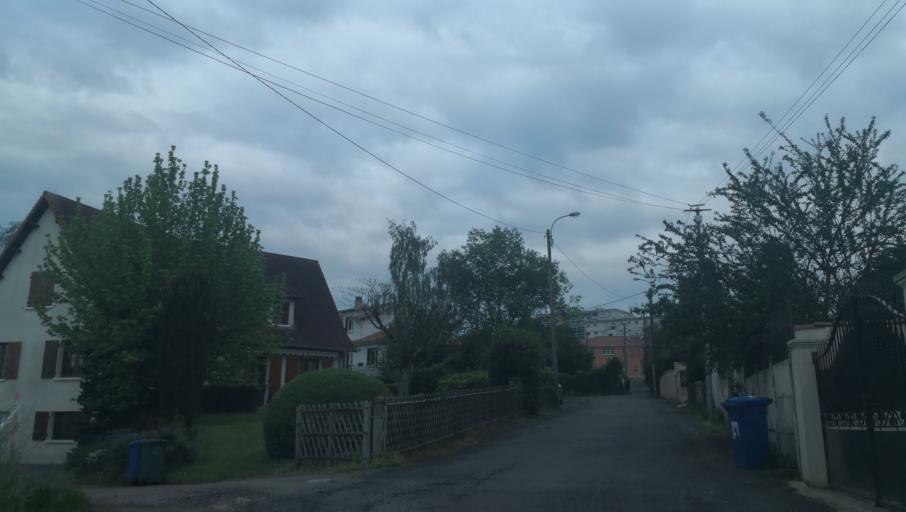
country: FR
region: Limousin
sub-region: Departement de la Haute-Vienne
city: Limoges
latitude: 45.8327
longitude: 1.2281
